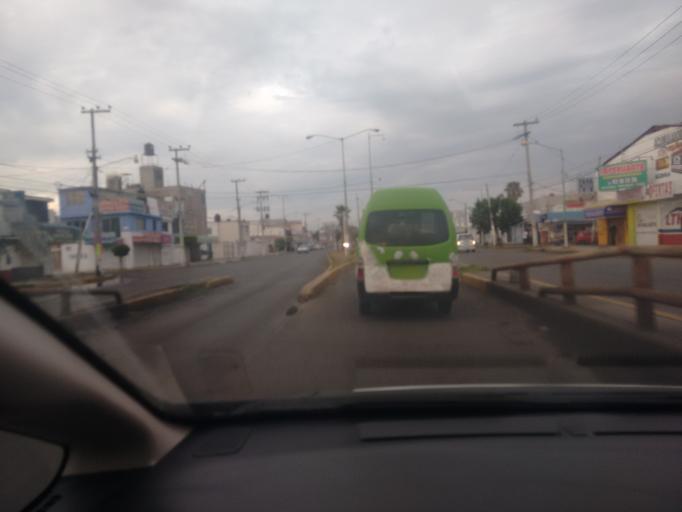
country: MX
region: Mexico City
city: Gustavo A. Madero
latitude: 19.4853
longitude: -99.0463
